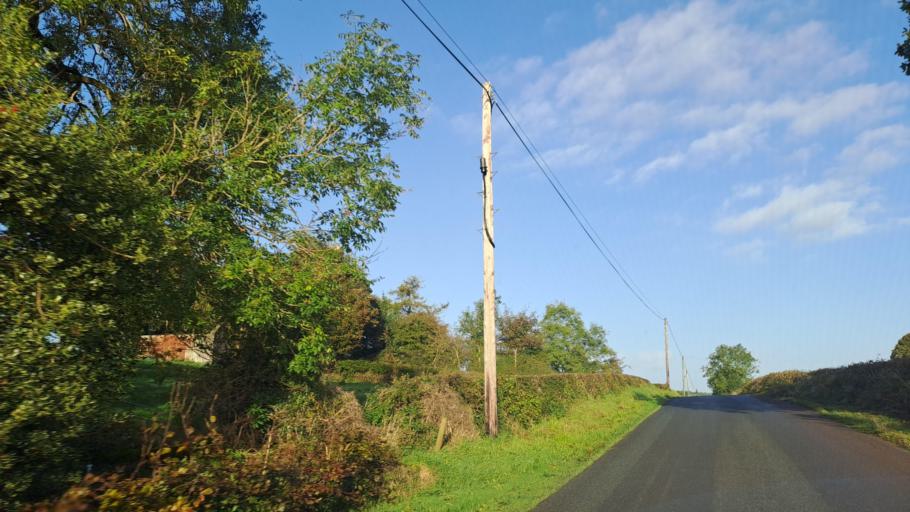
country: IE
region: Ulster
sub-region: County Monaghan
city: Castleblayney
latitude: 54.0634
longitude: -6.8242
